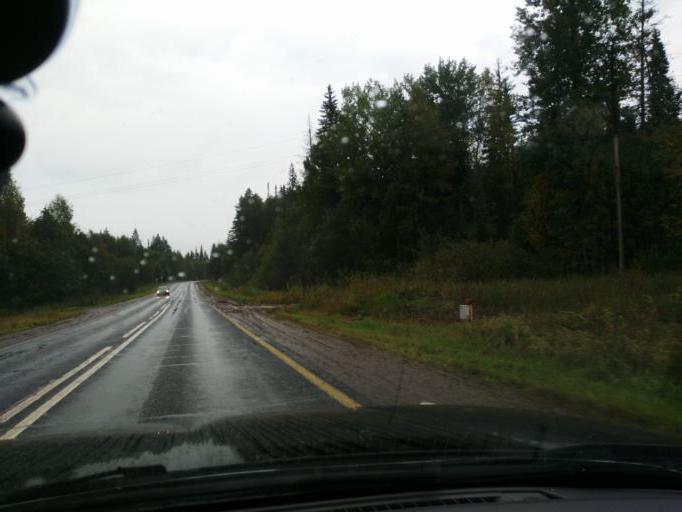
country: RU
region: Perm
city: Yugo-Kamskiy
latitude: 57.5241
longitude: 55.6845
